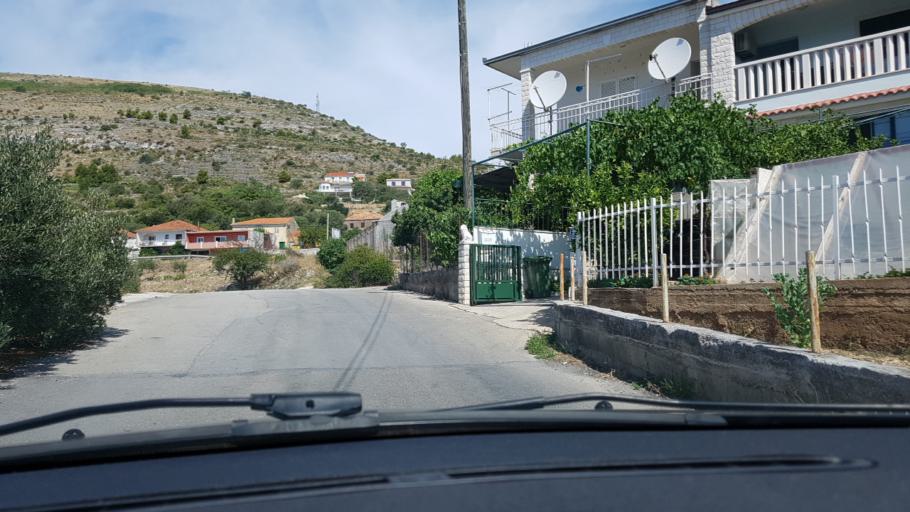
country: HR
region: Splitsko-Dalmatinska
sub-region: Grad Trogir
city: Trogir
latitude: 43.5221
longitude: 16.2268
